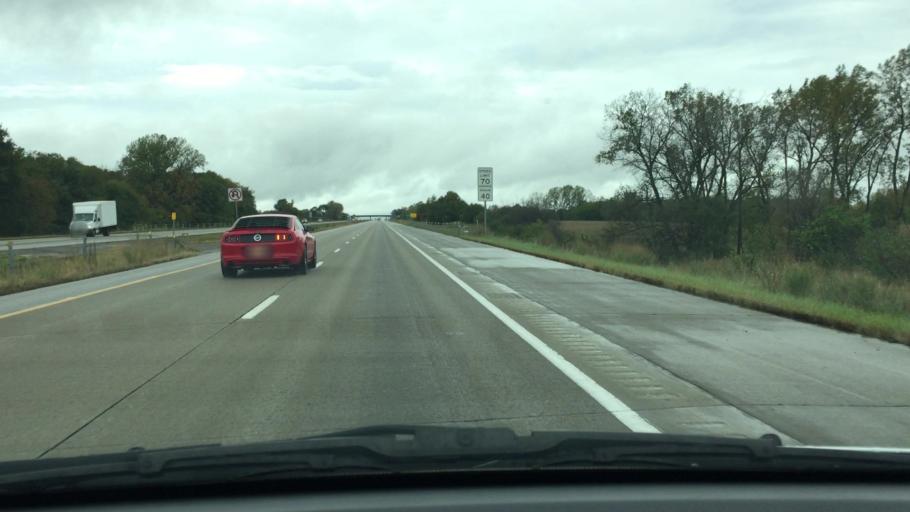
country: US
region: Iowa
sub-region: Polk County
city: Mitchellville
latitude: 41.6809
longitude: -93.3531
